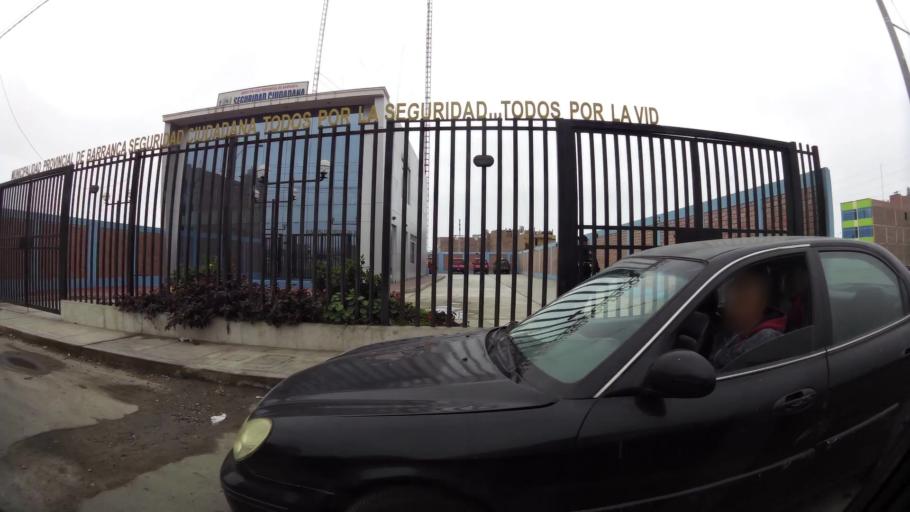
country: PE
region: Lima
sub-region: Barranca
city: Barranca
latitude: -10.7416
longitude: -77.7630
